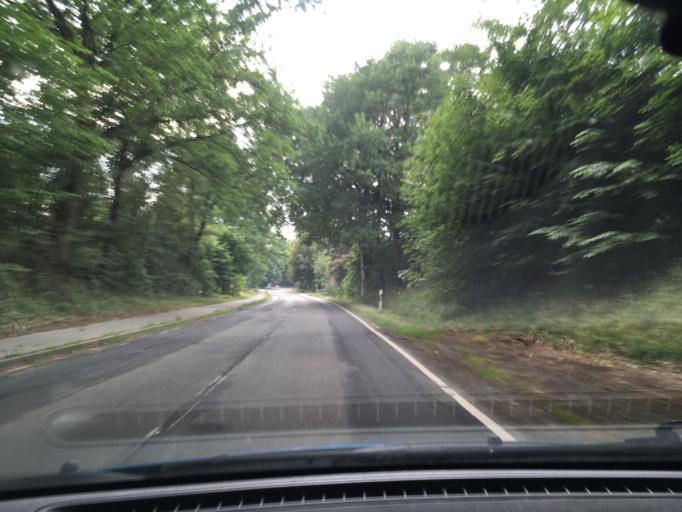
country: DE
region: Lower Saxony
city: Hollenstedt
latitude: 53.3625
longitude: 9.7206
